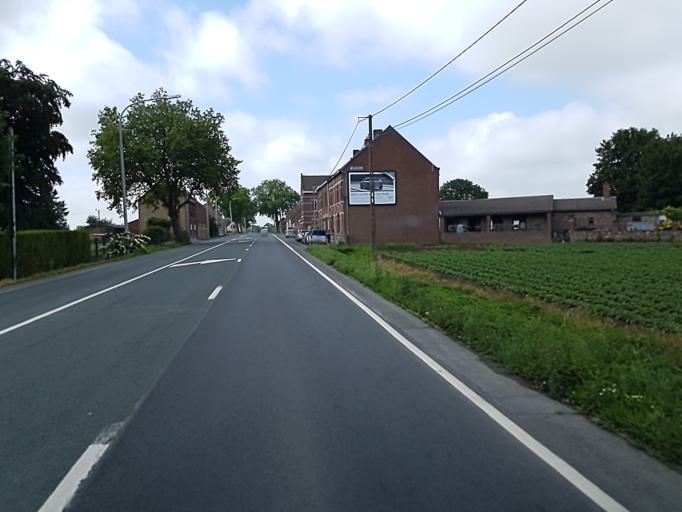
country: BE
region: Wallonia
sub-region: Province du Hainaut
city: Soignies
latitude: 50.5553
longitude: 4.0546
